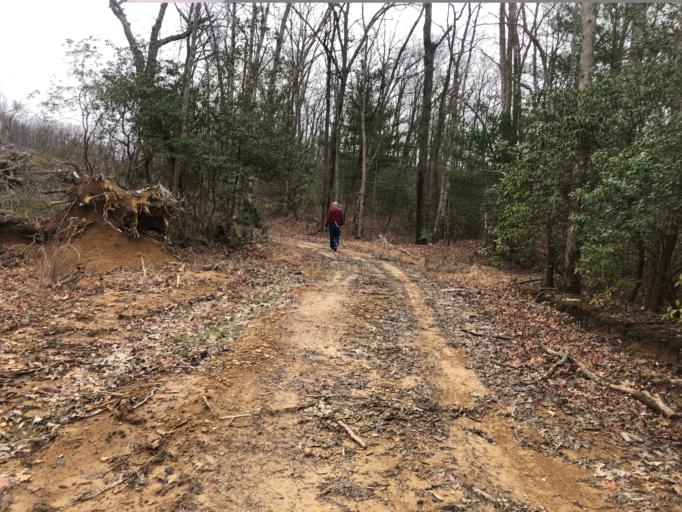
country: US
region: Tennessee
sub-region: Cumberland County
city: Fairfield Glade
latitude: 35.9699
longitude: -84.7652
